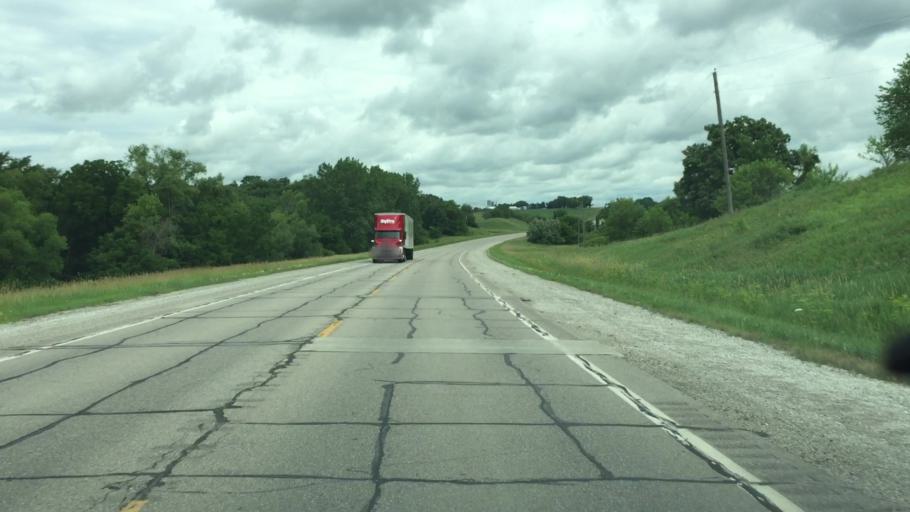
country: US
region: Iowa
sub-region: Jasper County
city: Monroe
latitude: 41.5324
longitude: -93.1019
